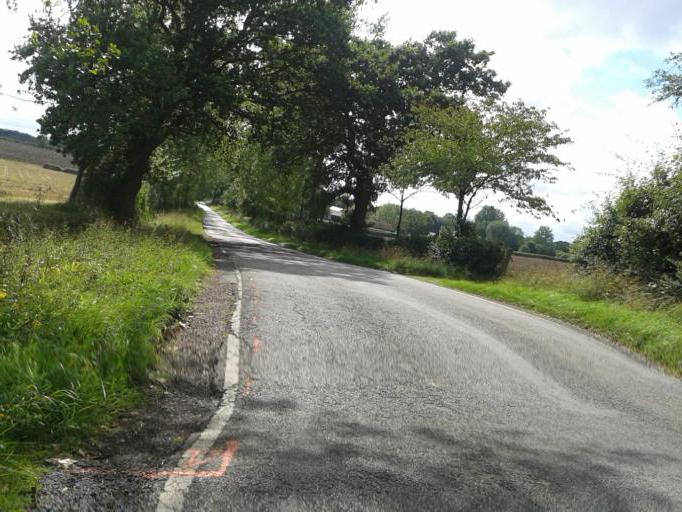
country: GB
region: England
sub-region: Cambridgeshire
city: Duxford
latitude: 52.0023
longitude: 0.1125
